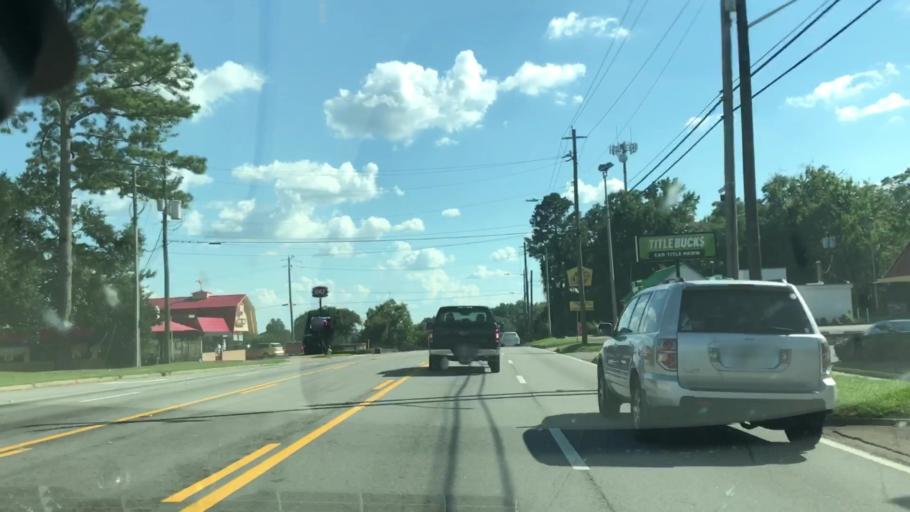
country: US
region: Georgia
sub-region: Troup County
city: La Grange
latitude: 33.0482
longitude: -85.0289
